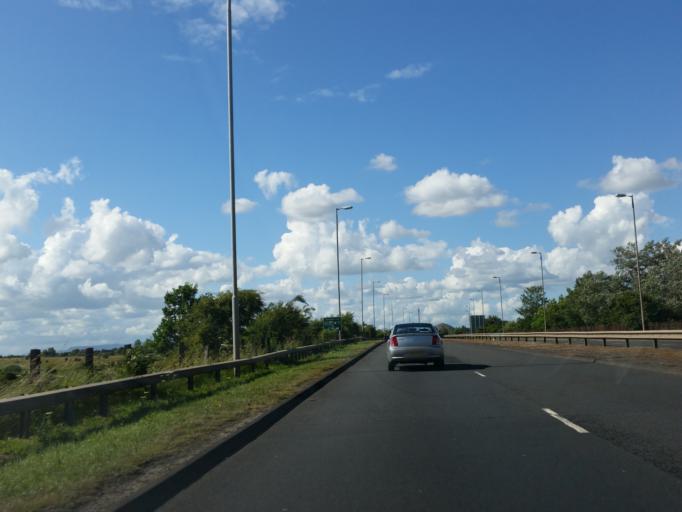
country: GB
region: Scotland
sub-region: North Lanarkshire
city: Bellshill
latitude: 55.8137
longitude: -4.0383
